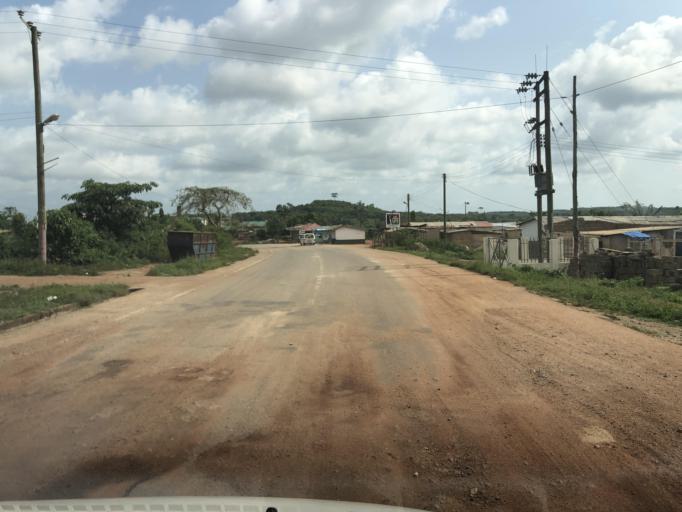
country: GH
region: Central
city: Elmina
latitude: 5.1956
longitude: -1.3198
